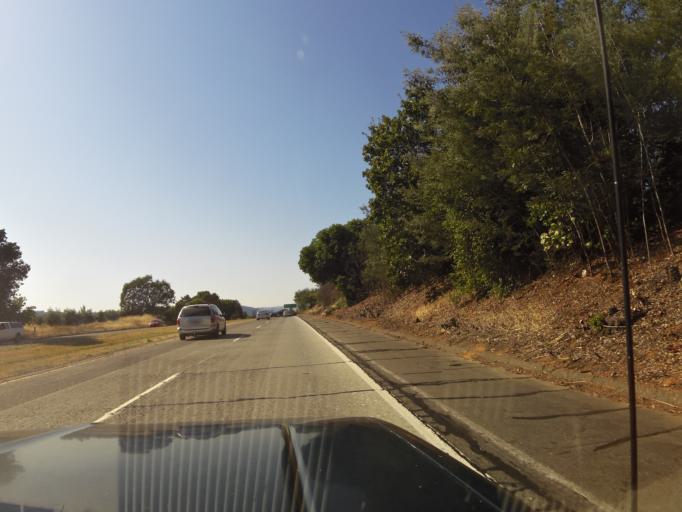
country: US
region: California
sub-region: Sonoma County
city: Cloverdale
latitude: 38.7541
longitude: -122.9696
